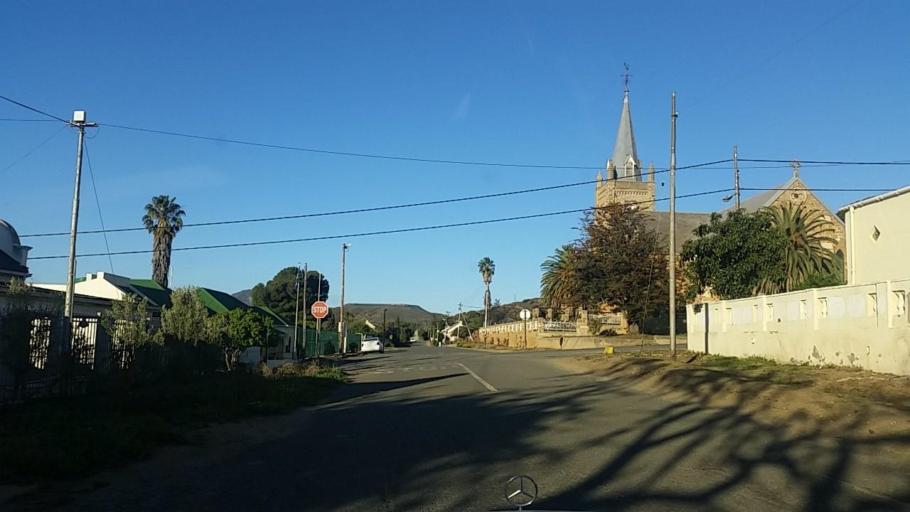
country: ZA
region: Western Cape
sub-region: Eden District Municipality
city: Knysna
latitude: -33.6584
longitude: 23.1258
